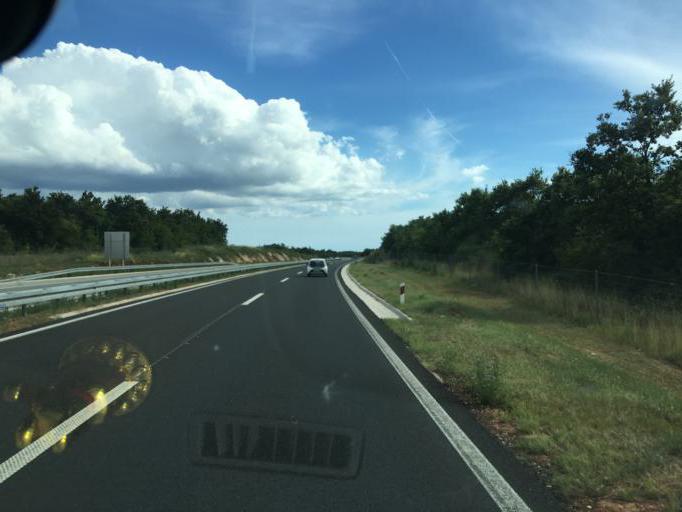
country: HR
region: Istarska
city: Vodnjan
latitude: 45.0414
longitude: 13.8319
